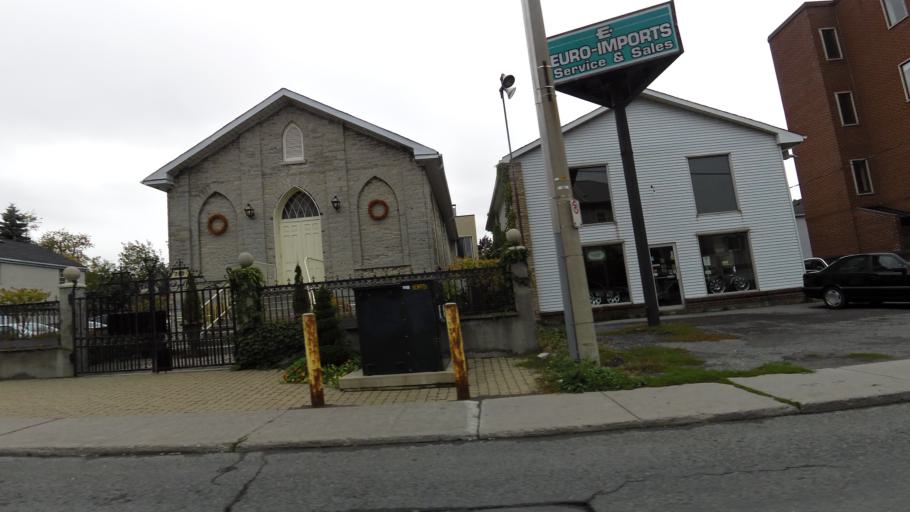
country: CA
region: Ontario
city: Kingston
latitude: 44.2338
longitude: -76.4911
